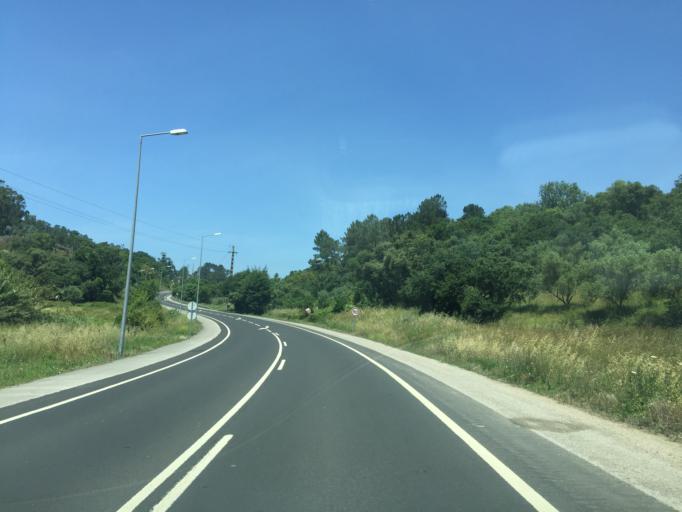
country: PT
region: Lisbon
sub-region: Mafra
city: Venda do Pinheiro
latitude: 38.8932
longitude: -9.2008
